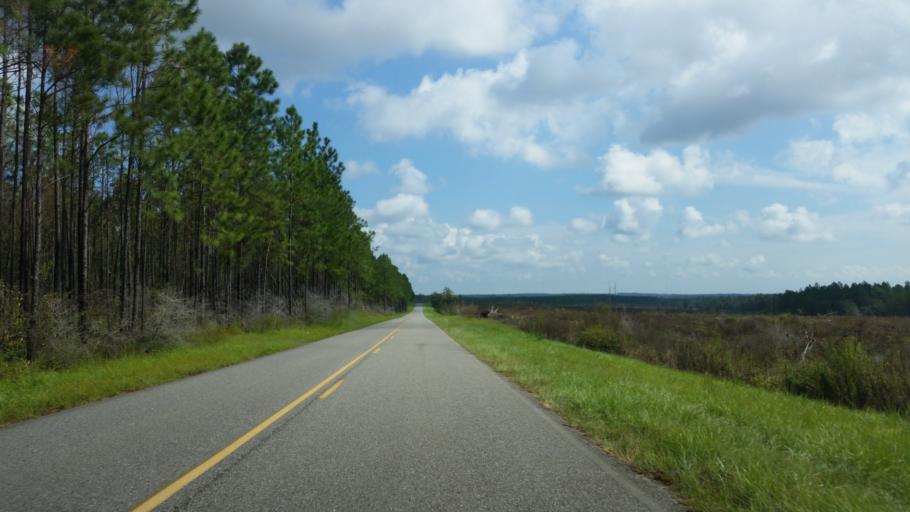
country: US
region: Florida
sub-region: Escambia County
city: Cantonment
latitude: 30.6811
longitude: -87.4688
